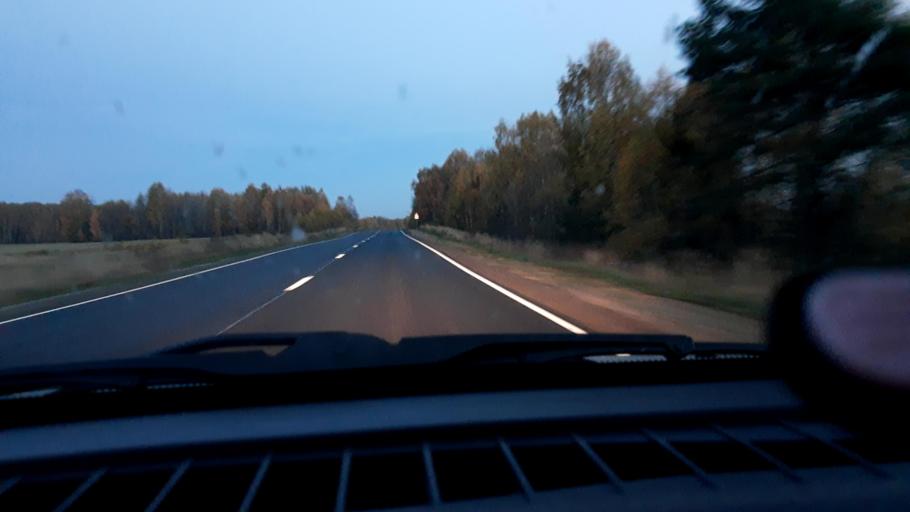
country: RU
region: Nizjnij Novgorod
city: Novaya Balakhna
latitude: 56.5788
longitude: 43.6919
